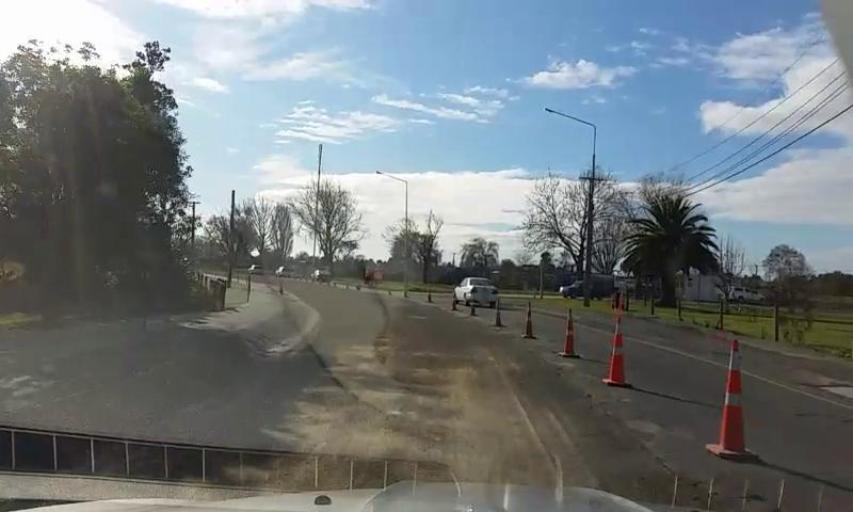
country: NZ
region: Canterbury
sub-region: Christchurch City
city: Christchurch
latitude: -43.5050
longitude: 172.6809
